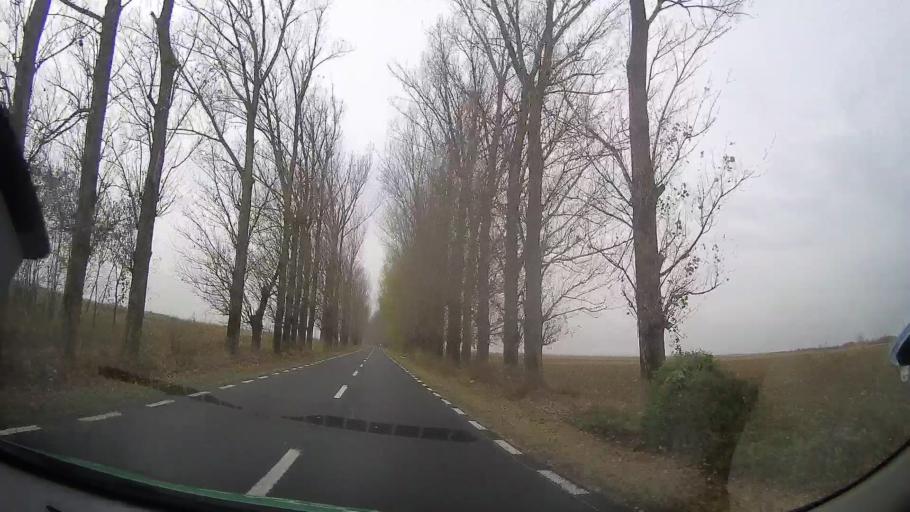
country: RO
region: Ilfov
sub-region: Comuna Nuci
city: Nuci
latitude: 44.7213
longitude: 26.2849
